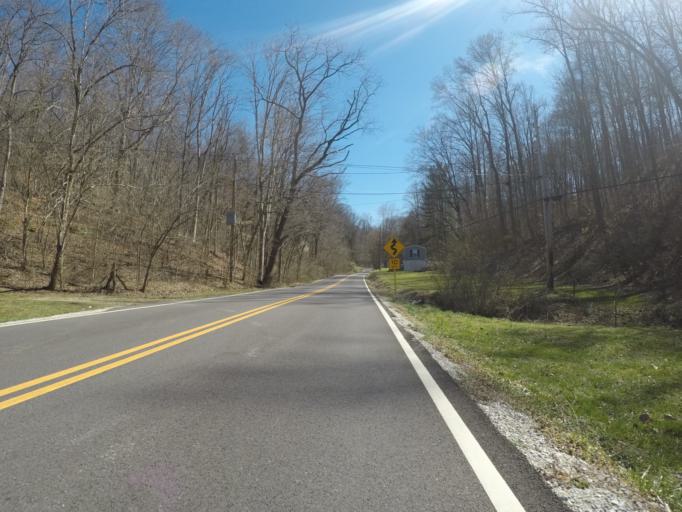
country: US
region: Ohio
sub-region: Lawrence County
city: South Point
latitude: 38.4613
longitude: -82.5570
